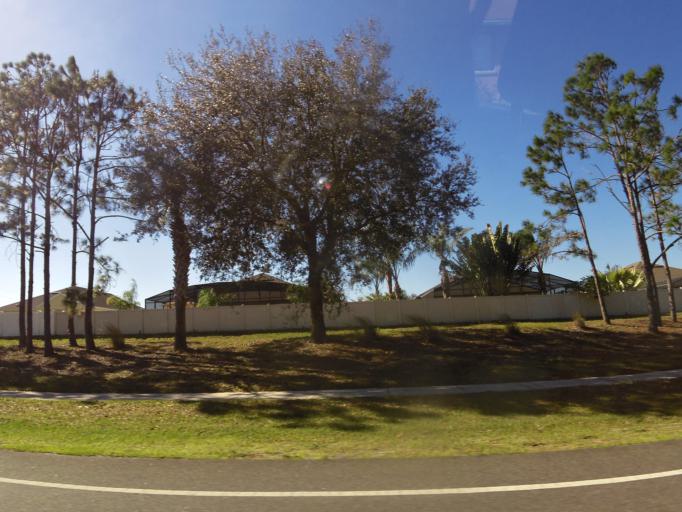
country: US
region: Florida
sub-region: Brevard County
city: Port Saint John
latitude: 28.5329
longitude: -80.8081
